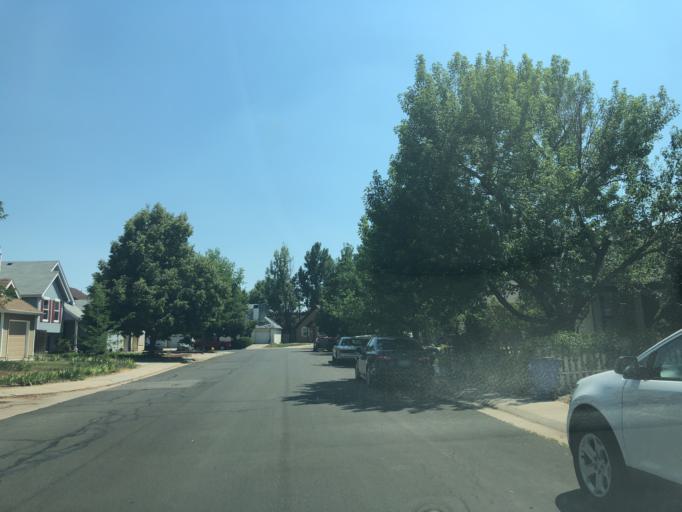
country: US
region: Colorado
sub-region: Arapahoe County
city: Dove Valley
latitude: 39.6327
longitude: -104.7908
